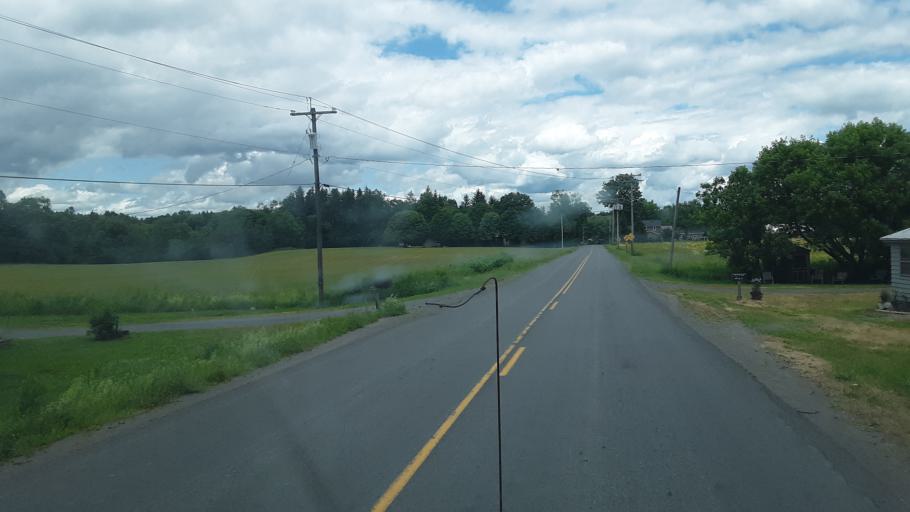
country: US
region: New York
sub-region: Oneida County
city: Rome
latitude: 43.3777
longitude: -75.5493
